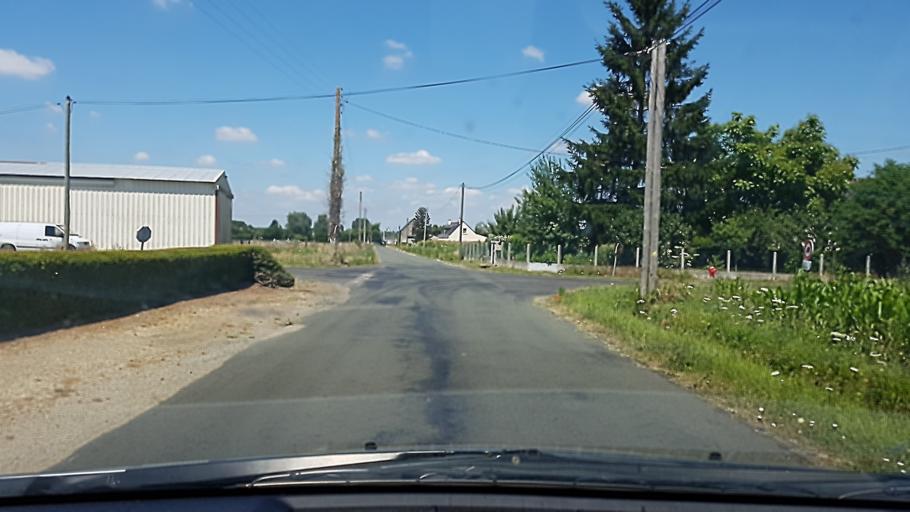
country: FR
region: Pays de la Loire
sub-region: Departement de Maine-et-Loire
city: Corze
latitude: 47.5449
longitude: -0.3895
